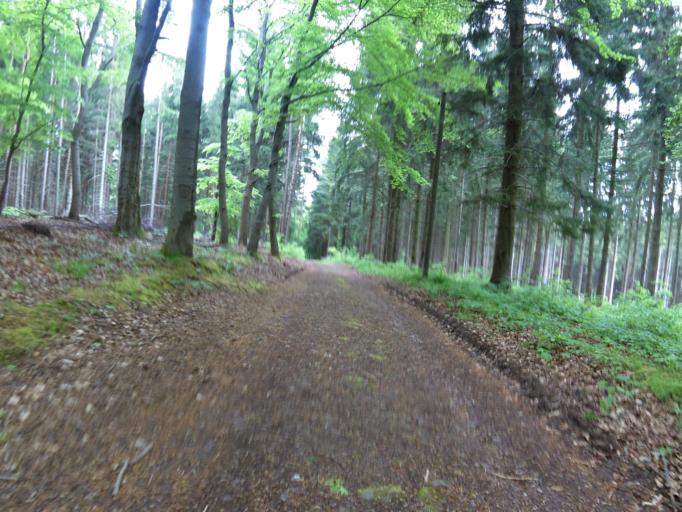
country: DE
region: Thuringia
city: Georgenthal
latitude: 50.8134
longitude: 10.6727
